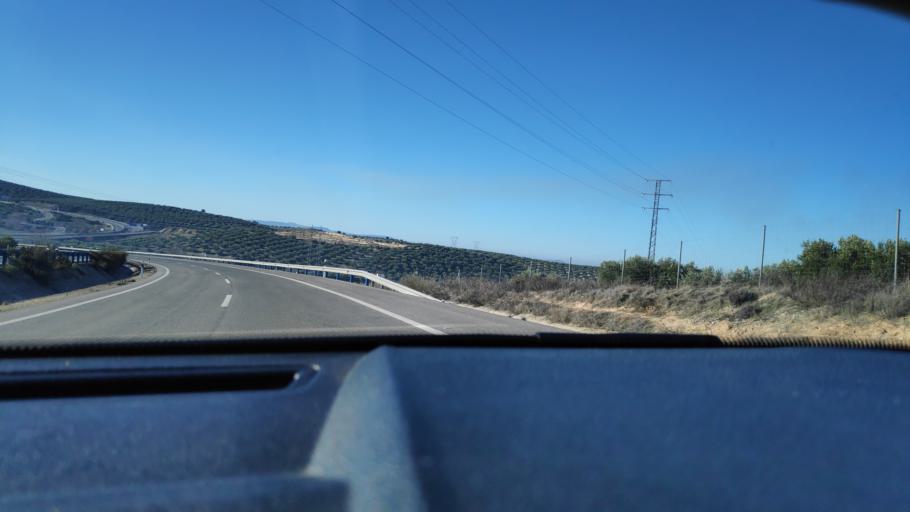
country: ES
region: Andalusia
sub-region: Provincia de Jaen
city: Martos
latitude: 37.7279
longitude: -3.9795
